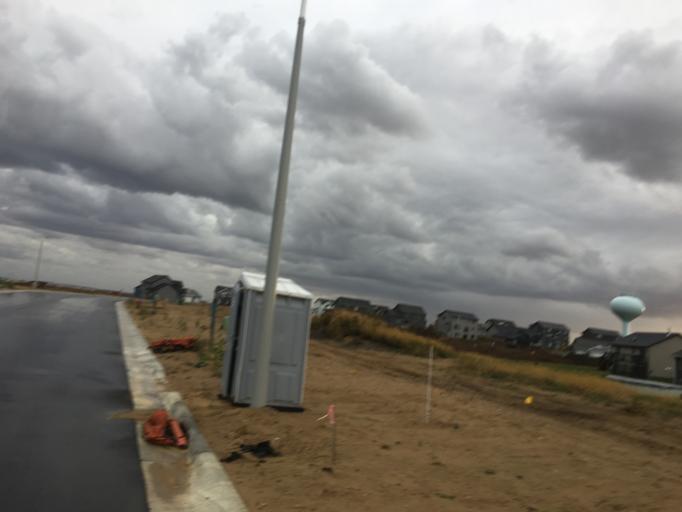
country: US
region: Minnesota
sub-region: Olmsted County
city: Oronoco
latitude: 44.0928
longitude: -92.5244
